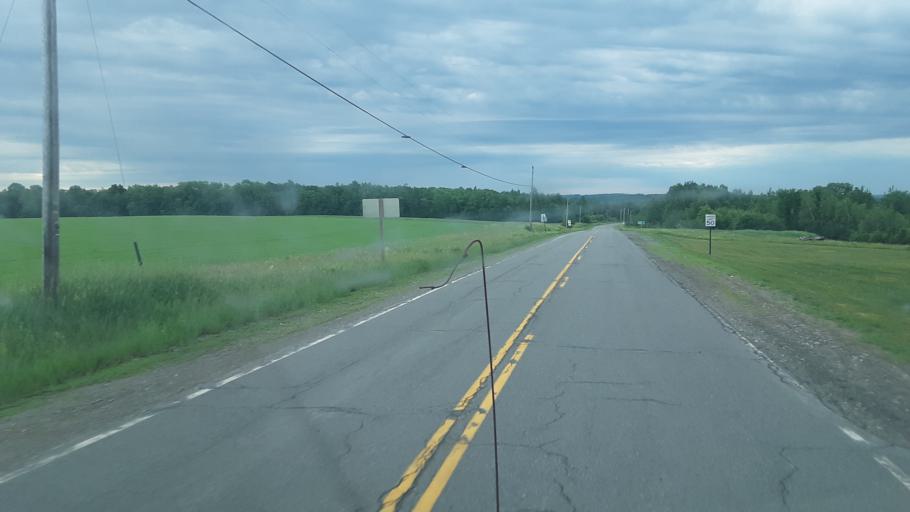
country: US
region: Maine
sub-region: Penobscot County
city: Patten
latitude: 45.8695
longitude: -68.3299
